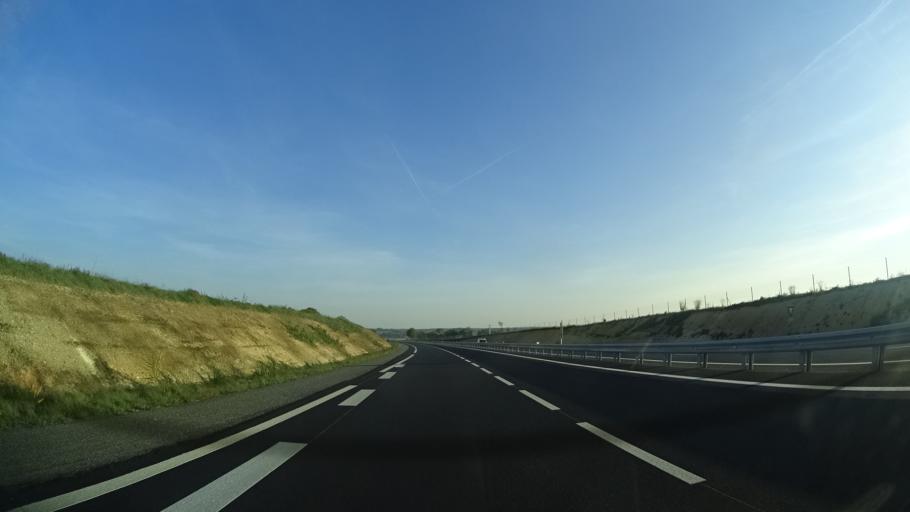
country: FR
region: Brittany
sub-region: Departement d'Ille-et-Vilaine
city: Pipriac
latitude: 47.8133
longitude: -1.9202
